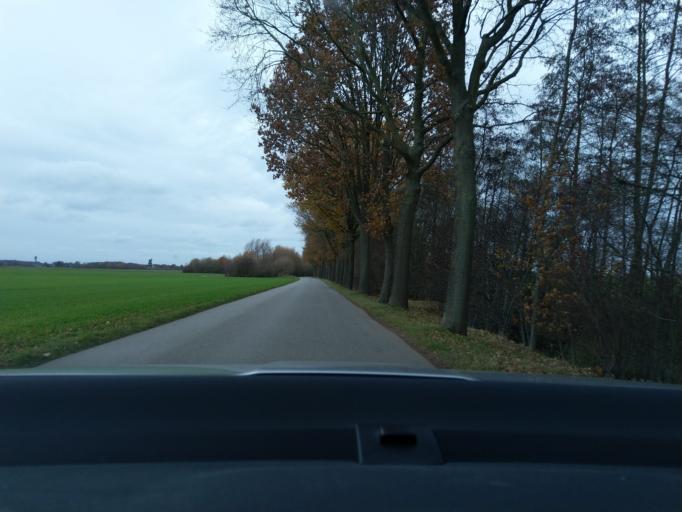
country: DE
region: North Rhine-Westphalia
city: Erkelenz
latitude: 51.1176
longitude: 6.3275
